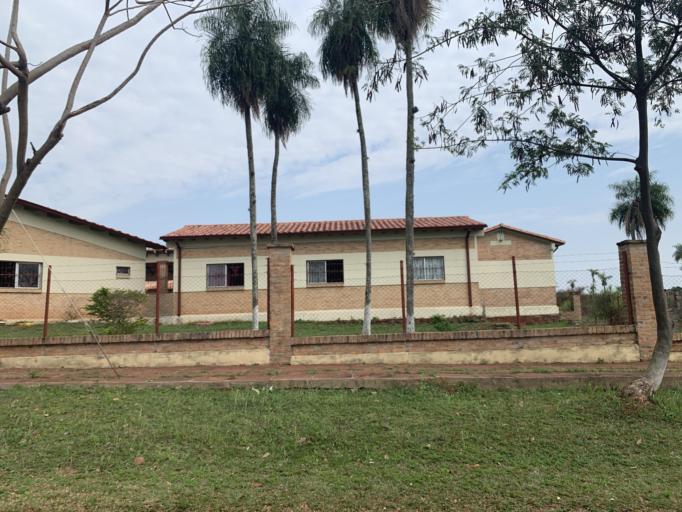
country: PY
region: Misiones
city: San Juan Bautista
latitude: -26.6657
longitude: -57.1553
